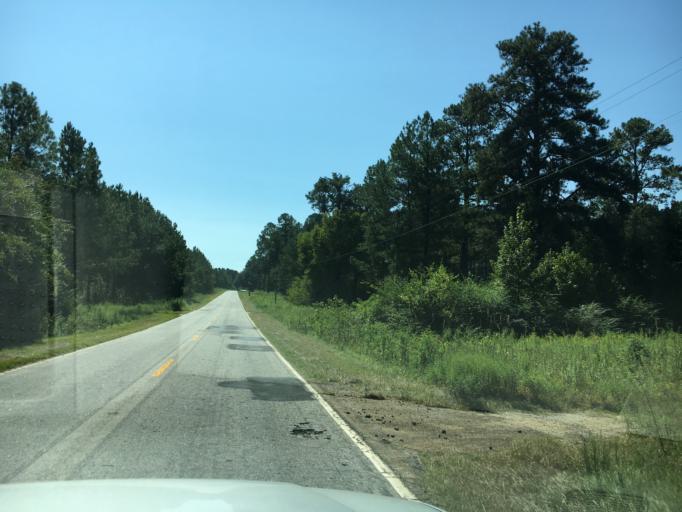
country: US
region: South Carolina
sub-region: Laurens County
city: Joanna
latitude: 34.3303
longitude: -81.8513
